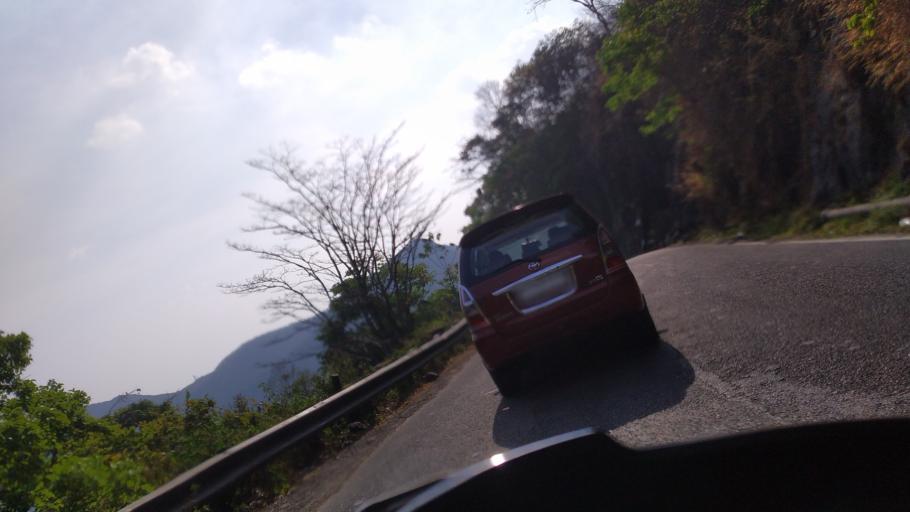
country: IN
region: Kerala
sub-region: Kottayam
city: Erattupetta
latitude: 9.5603
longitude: 76.9822
